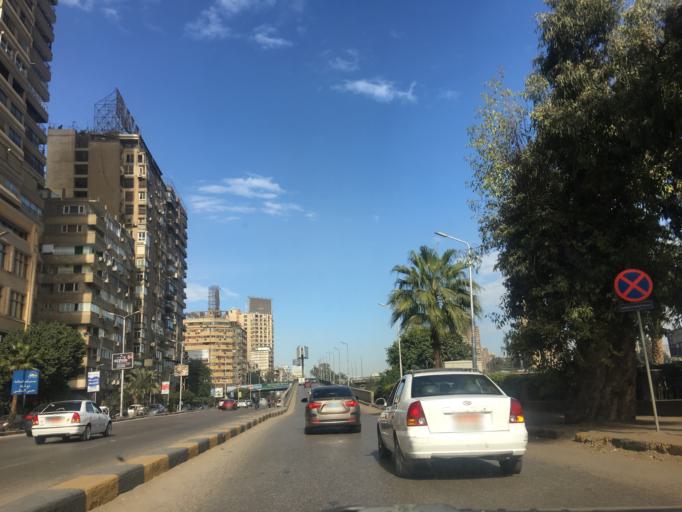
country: EG
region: Muhafazat al Qahirah
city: Cairo
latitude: 30.0461
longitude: 31.2185
